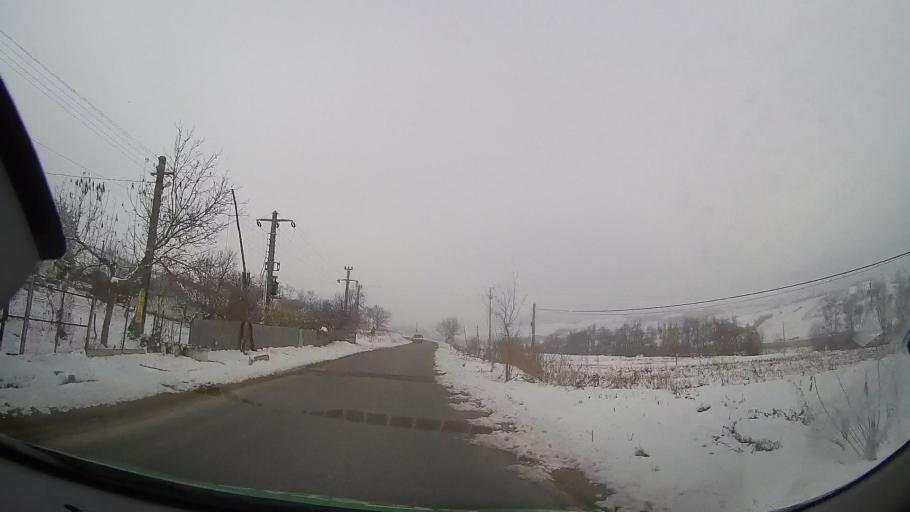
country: RO
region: Bacau
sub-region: Comuna Vultureni
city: Vultureni
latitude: 46.3804
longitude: 27.2760
